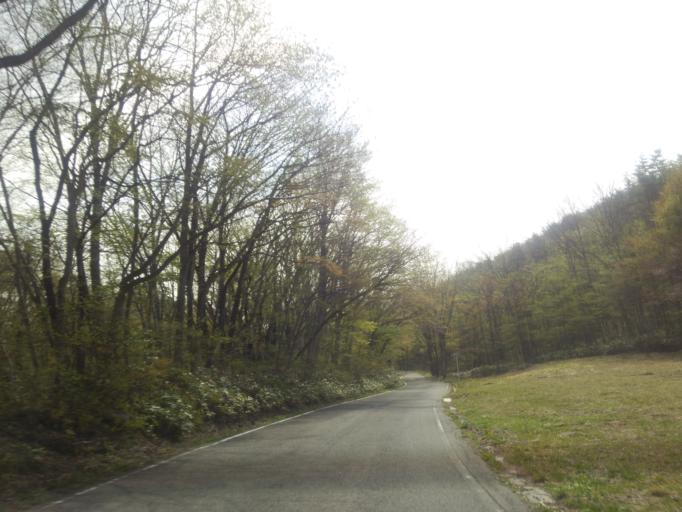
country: JP
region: Fukushima
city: Nihommatsu
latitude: 37.6410
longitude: 140.3332
